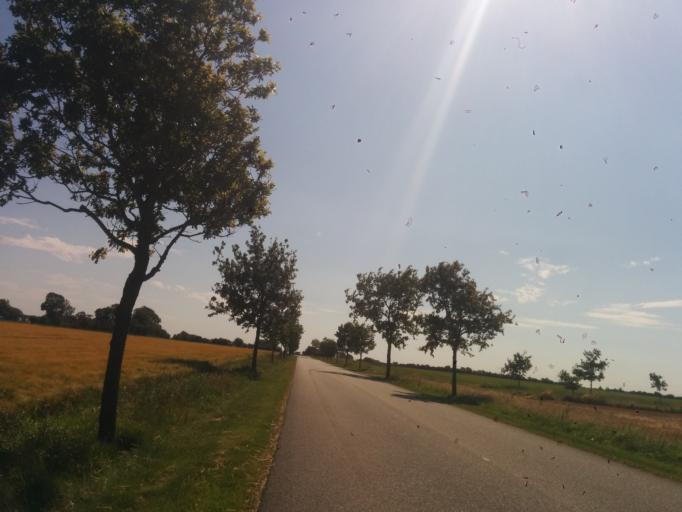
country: DK
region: Central Jutland
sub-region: Viborg Kommune
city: Bjerringbro
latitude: 56.4784
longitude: 9.5763
